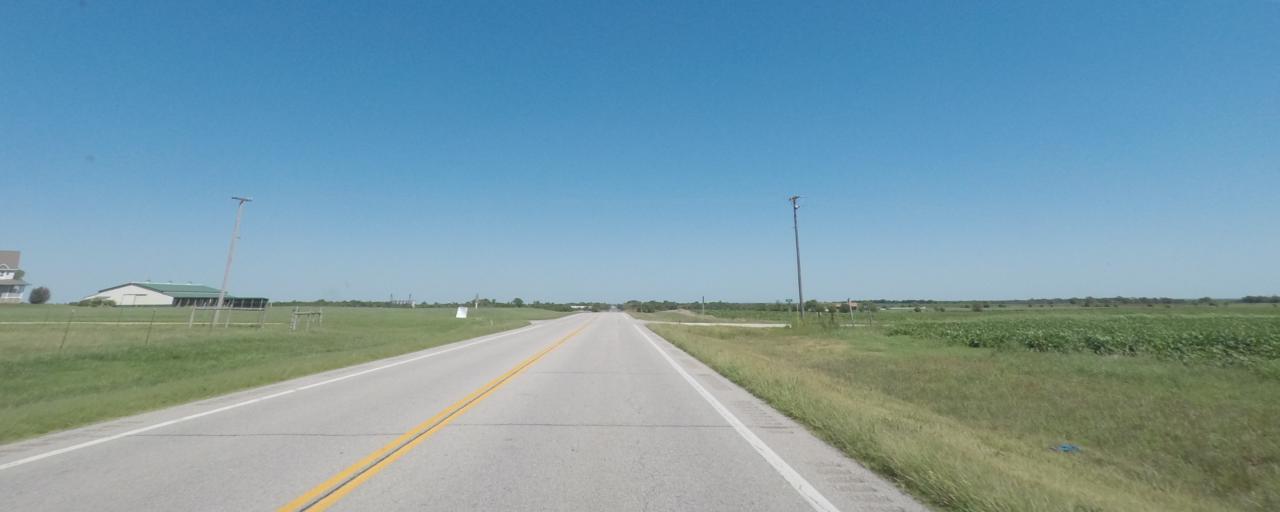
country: US
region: Kansas
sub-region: Sumner County
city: Wellington
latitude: 37.3614
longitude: -97.3850
